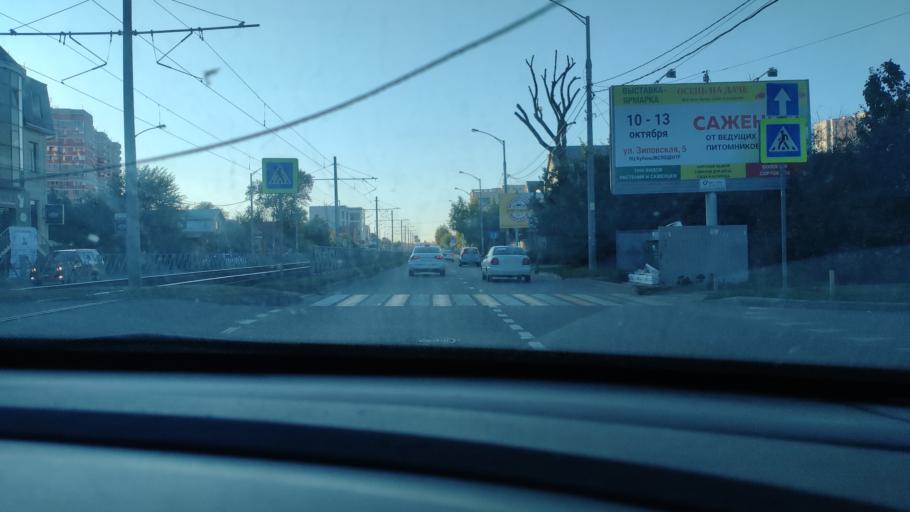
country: RU
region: Krasnodarskiy
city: Krasnodar
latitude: 45.0405
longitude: 38.9538
